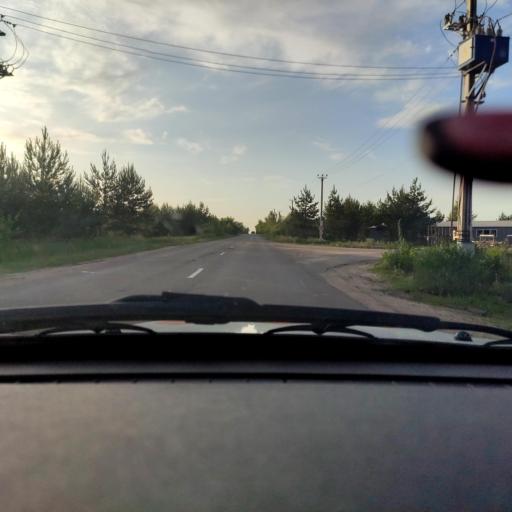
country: RU
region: Voronezj
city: Podgornoye
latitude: 51.8311
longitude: 39.2056
